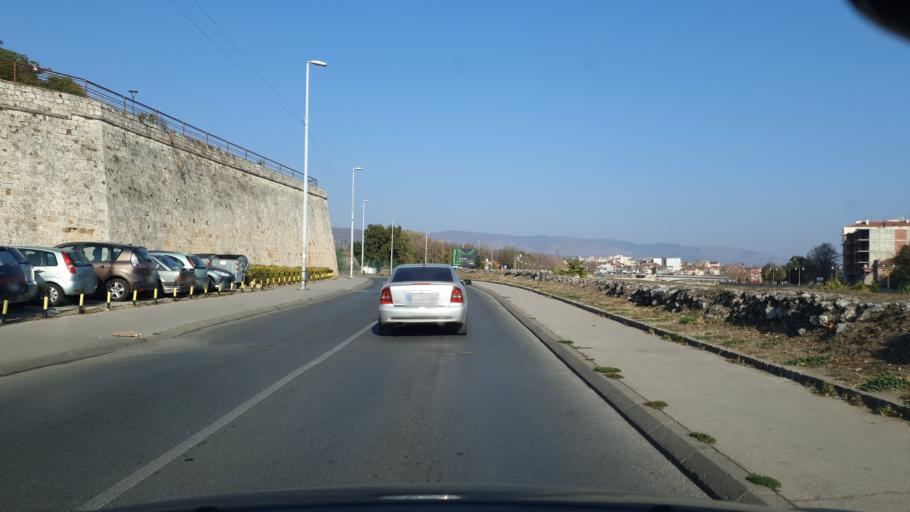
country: RS
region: Central Serbia
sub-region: Nisavski Okrug
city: Nis
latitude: 43.3241
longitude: 21.8973
